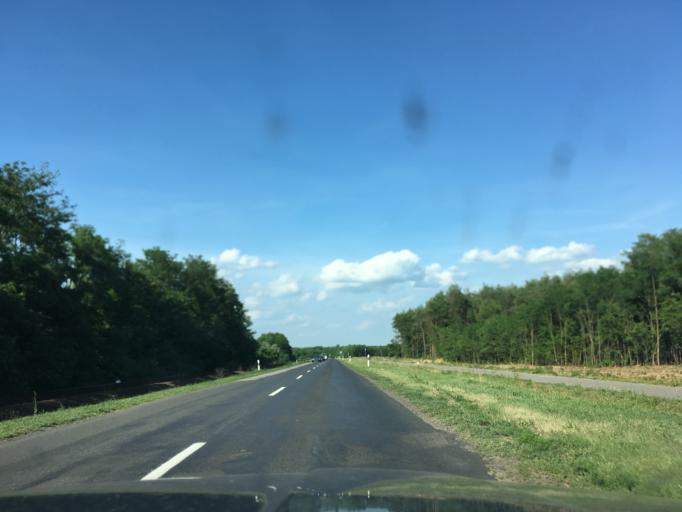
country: HU
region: Hajdu-Bihar
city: Hajdusamson
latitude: 47.6234
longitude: 21.7828
